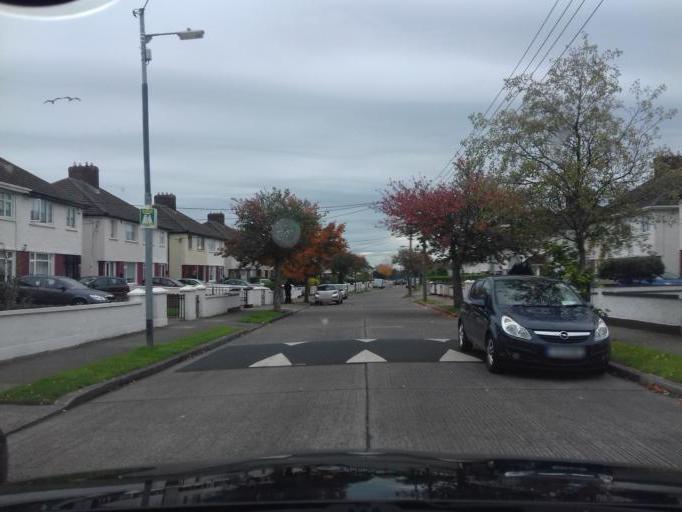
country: IE
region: Leinster
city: Artane
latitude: 53.3804
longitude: -6.2261
